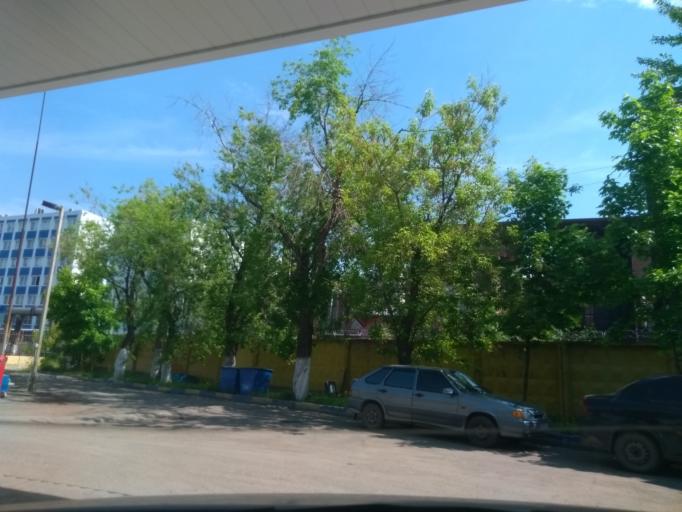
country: RU
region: Perm
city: Perm
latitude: 57.9818
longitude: 56.2473
